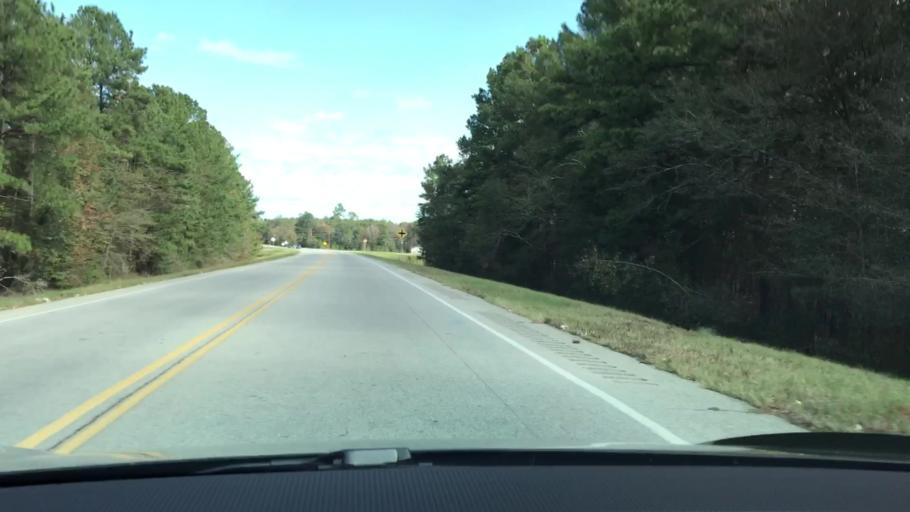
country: US
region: Georgia
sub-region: Jefferson County
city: Louisville
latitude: 32.9607
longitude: -82.3912
